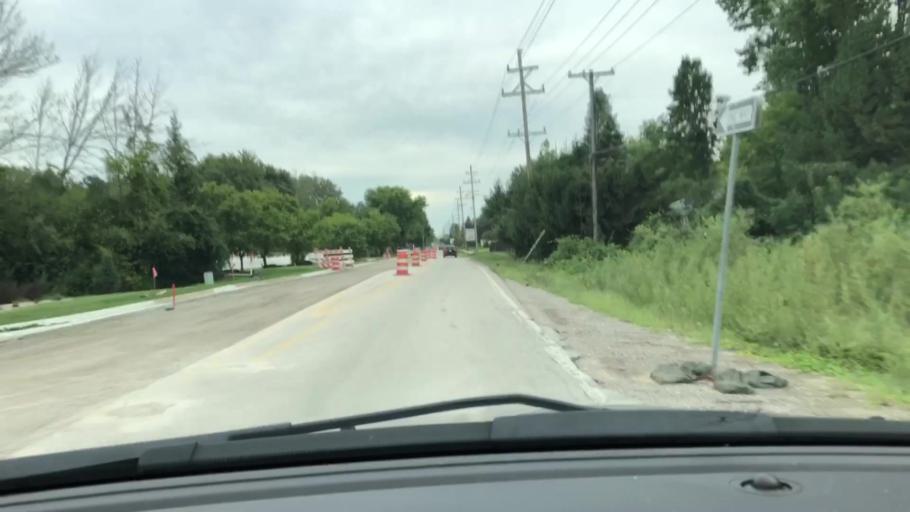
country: US
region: Michigan
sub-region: Midland County
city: Midland
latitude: 43.6354
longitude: -84.1872
